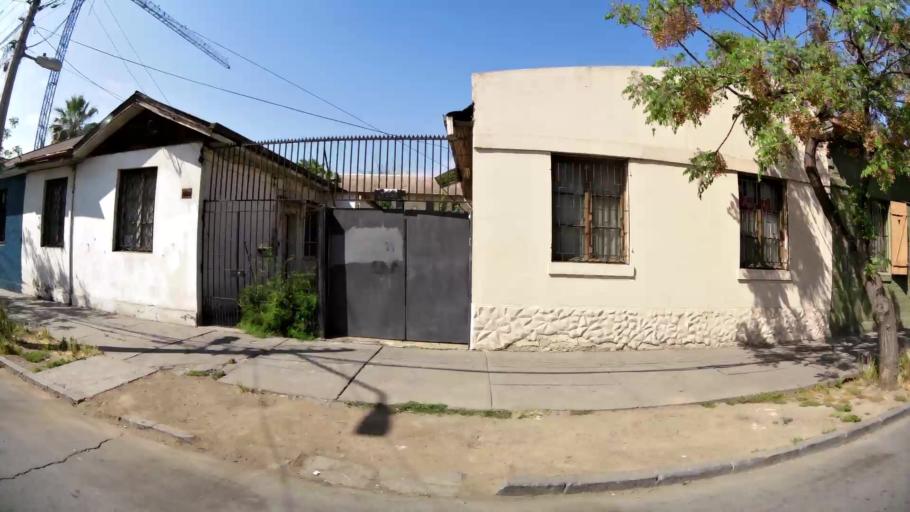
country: CL
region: Santiago Metropolitan
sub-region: Provincia de Santiago
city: Santiago
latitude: -33.4037
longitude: -70.6628
